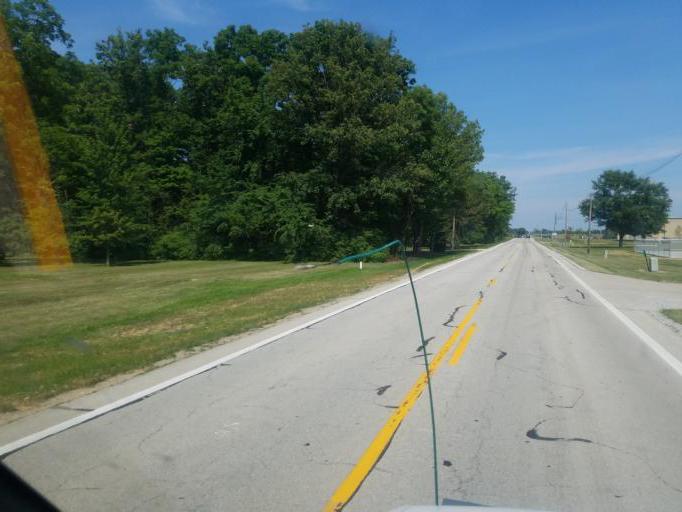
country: US
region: Ohio
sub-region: Auglaize County
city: New Bremen
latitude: 40.4961
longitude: -84.3017
